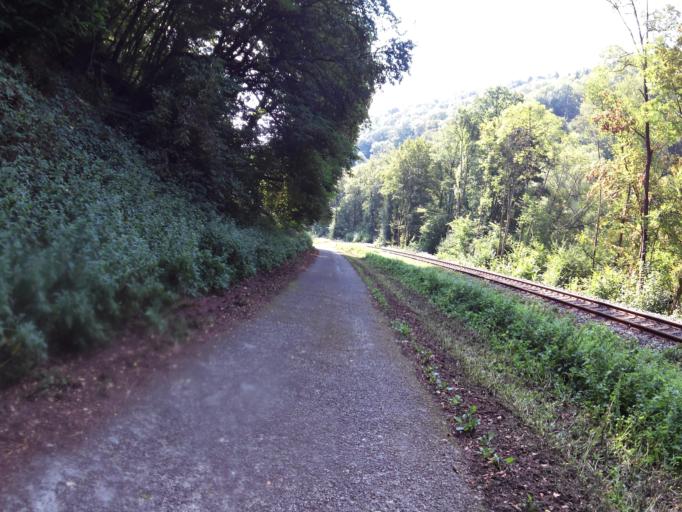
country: DE
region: Rheinland-Pfalz
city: Hosten
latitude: 49.8815
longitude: 6.6015
